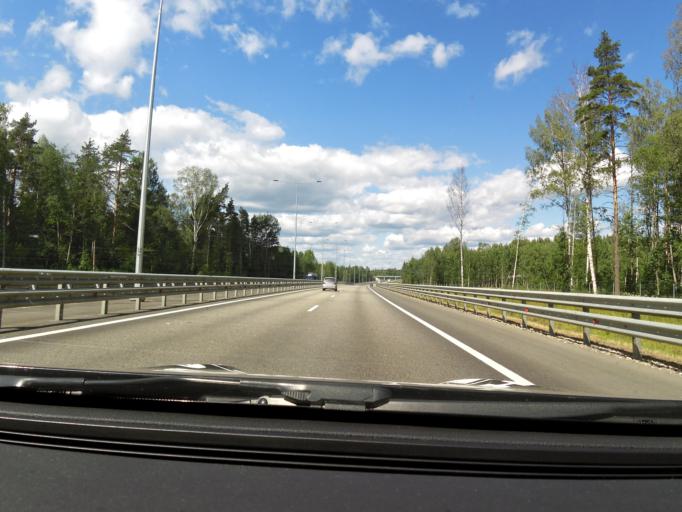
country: RU
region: Tverskaya
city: Vyshniy Volochek
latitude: 57.3789
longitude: 34.5755
